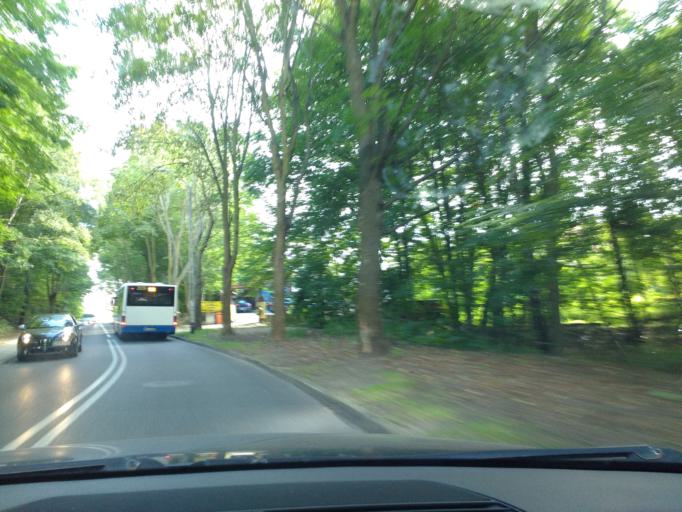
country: PL
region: Pomeranian Voivodeship
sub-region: Gdynia
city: Gdynia
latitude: 54.5041
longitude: 18.5136
